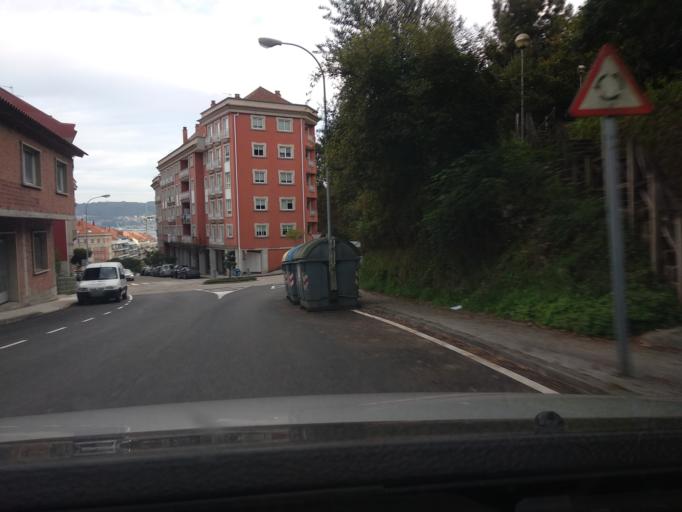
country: ES
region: Galicia
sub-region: Provincia de Pontevedra
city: Moana
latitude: 42.2903
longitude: -8.7378
